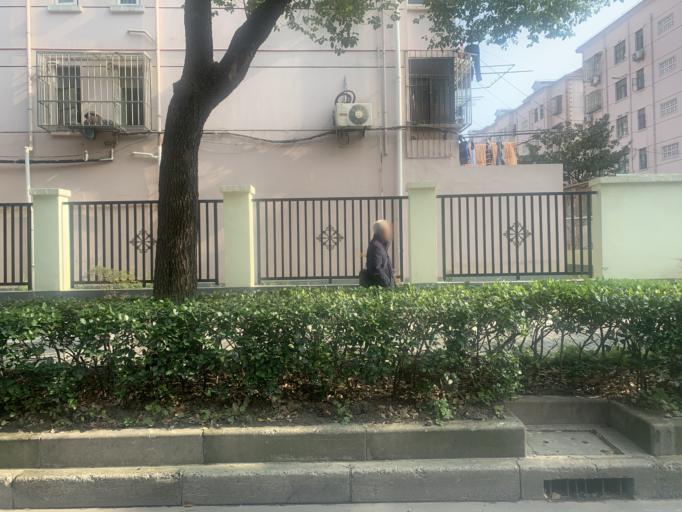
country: CN
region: Shanghai Shi
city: Huamu
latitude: 31.1851
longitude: 121.5148
